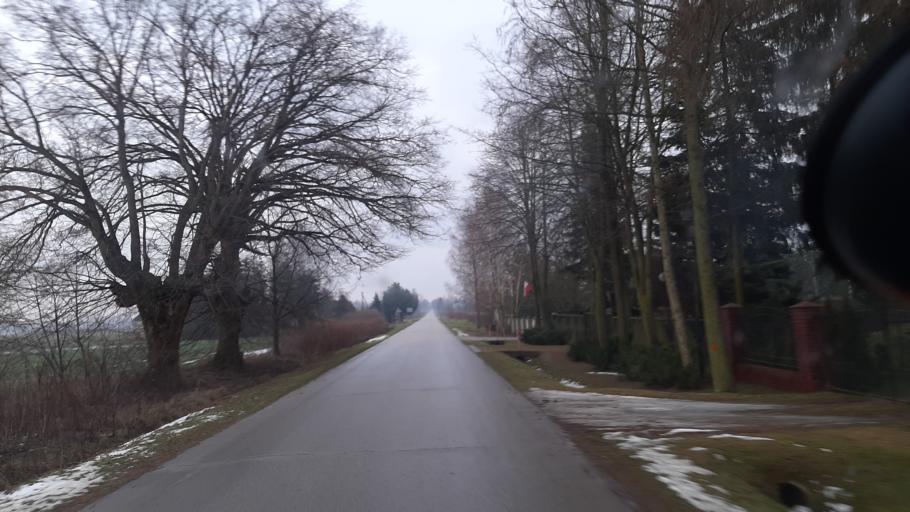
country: PL
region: Lublin Voivodeship
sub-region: Powiat lubelski
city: Lublin
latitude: 51.3397
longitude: 22.5383
